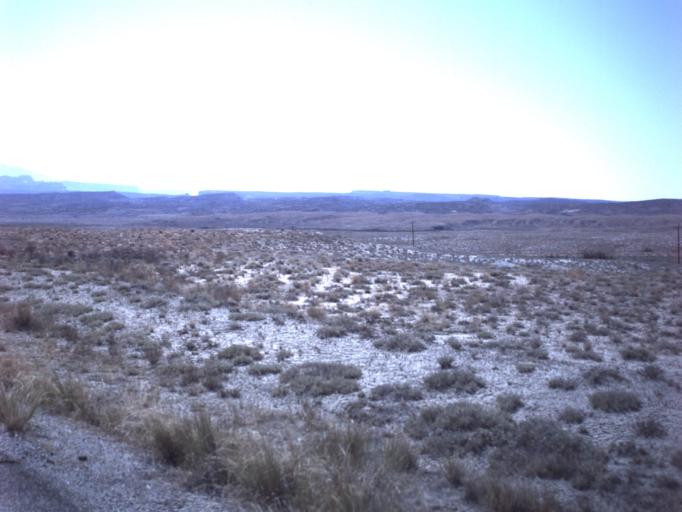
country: US
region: Utah
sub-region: Grand County
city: Moab
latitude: 38.9004
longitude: -109.3140
